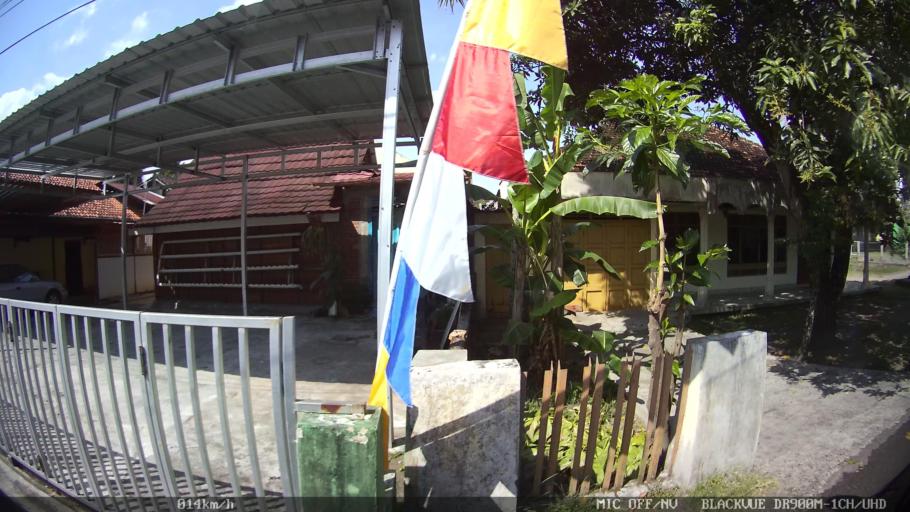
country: ID
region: Daerah Istimewa Yogyakarta
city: Kasihan
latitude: -7.8224
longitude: 110.3691
